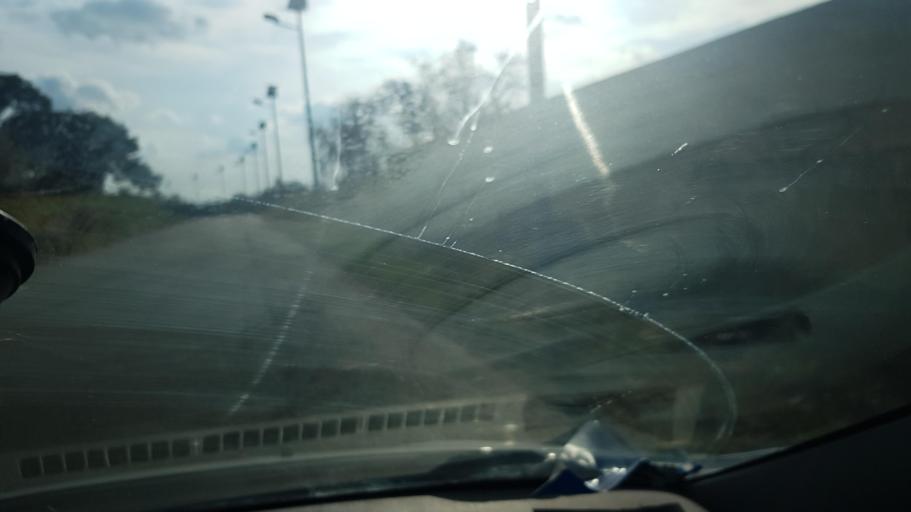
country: IT
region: Apulia
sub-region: Provincia di Brindisi
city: Cellino San Marco
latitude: 40.4635
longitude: 17.9589
